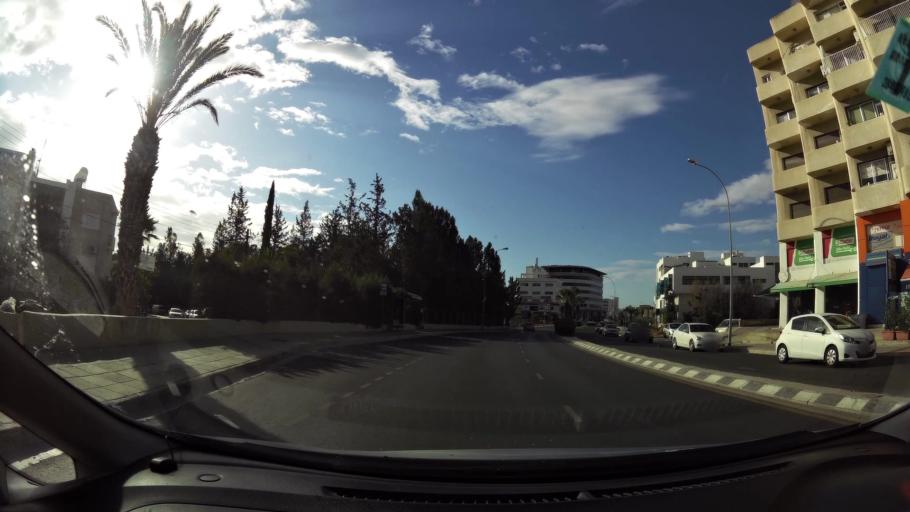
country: CY
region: Lefkosia
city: Nicosia
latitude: 35.1476
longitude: 33.3601
